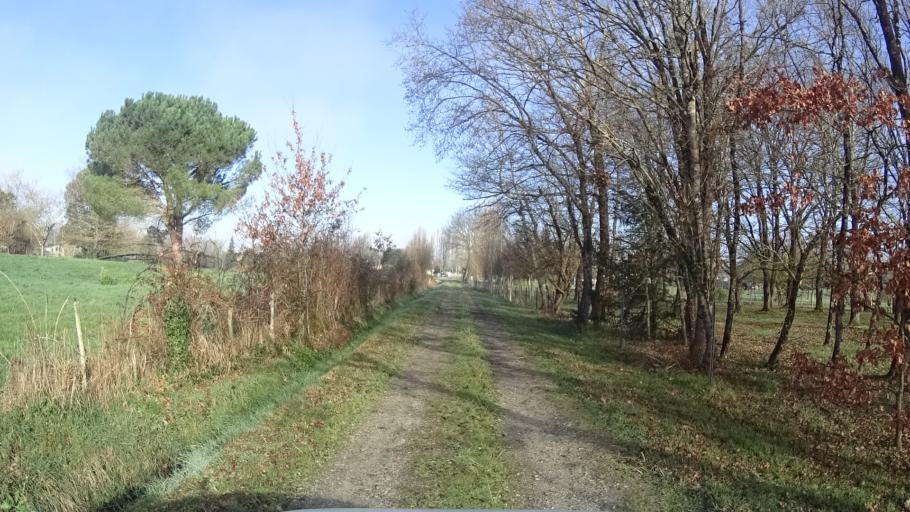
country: FR
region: Poitou-Charentes
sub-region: Departement de la Charente-Maritime
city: Saint-Aigulin
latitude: 45.1517
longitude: -0.0029
